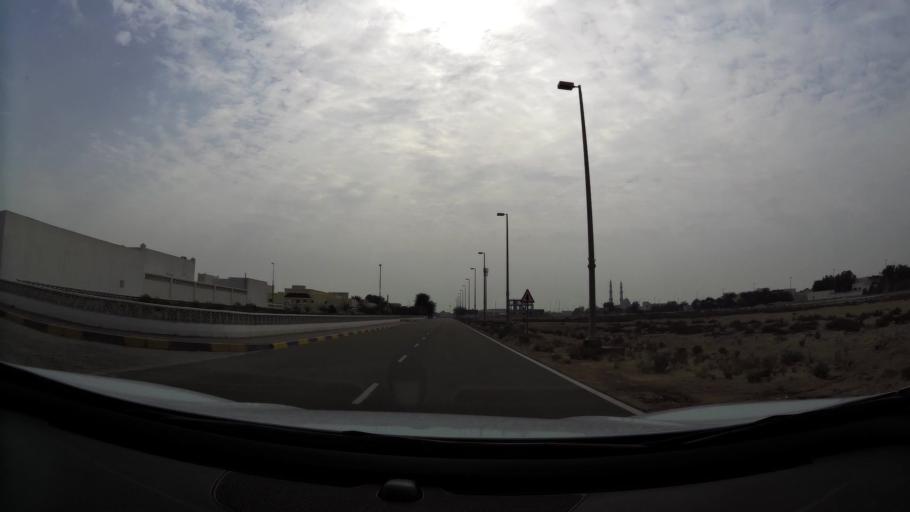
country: AE
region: Abu Dhabi
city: Abu Dhabi
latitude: 24.6778
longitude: 54.7558
